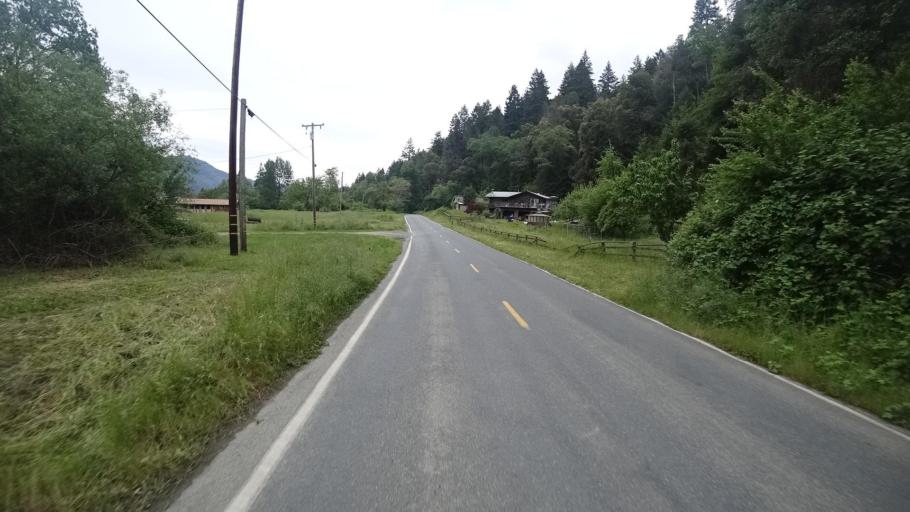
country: US
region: California
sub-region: Humboldt County
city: Willow Creek
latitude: 41.0623
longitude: -123.6942
